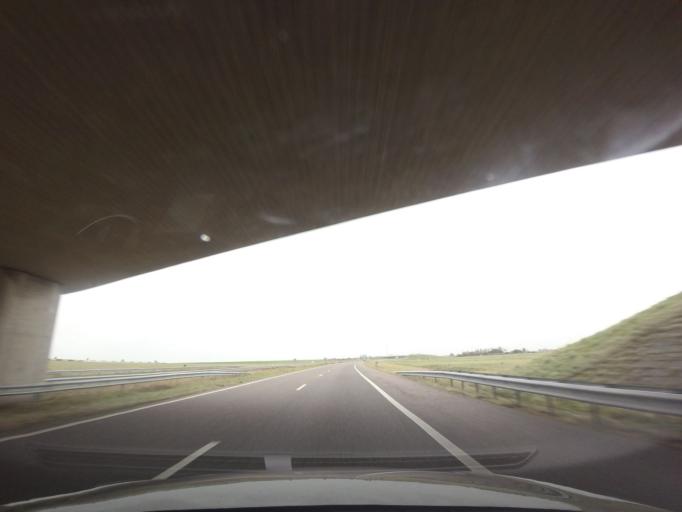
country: NL
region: Friesland
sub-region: Sudwest Fryslan
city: Makkum
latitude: 53.1019
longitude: 5.3846
